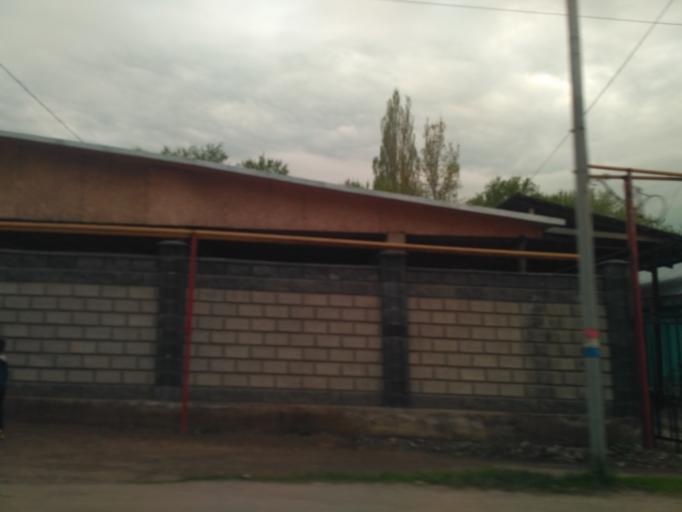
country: KZ
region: Almaty Oblysy
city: Burunday
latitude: 43.2109
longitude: 76.3242
